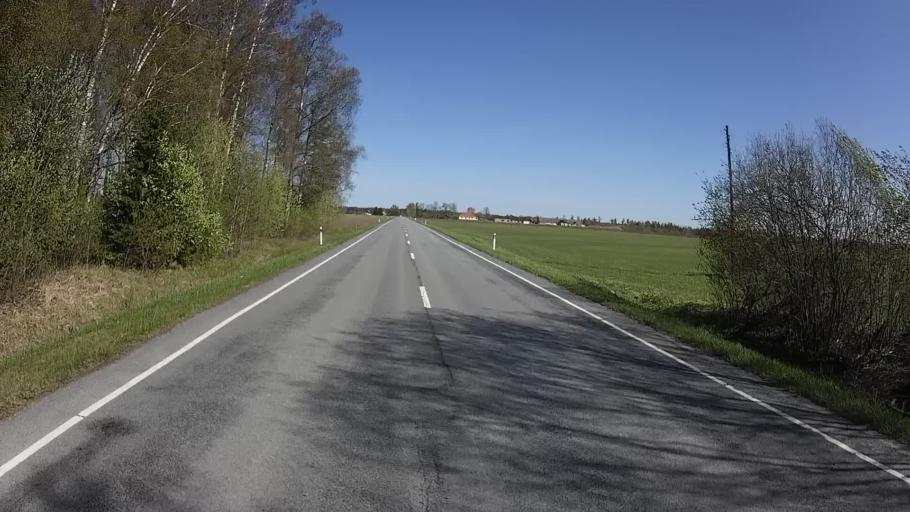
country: EE
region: Raplamaa
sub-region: Jaervakandi vald
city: Jarvakandi
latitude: 58.8359
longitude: 24.7969
